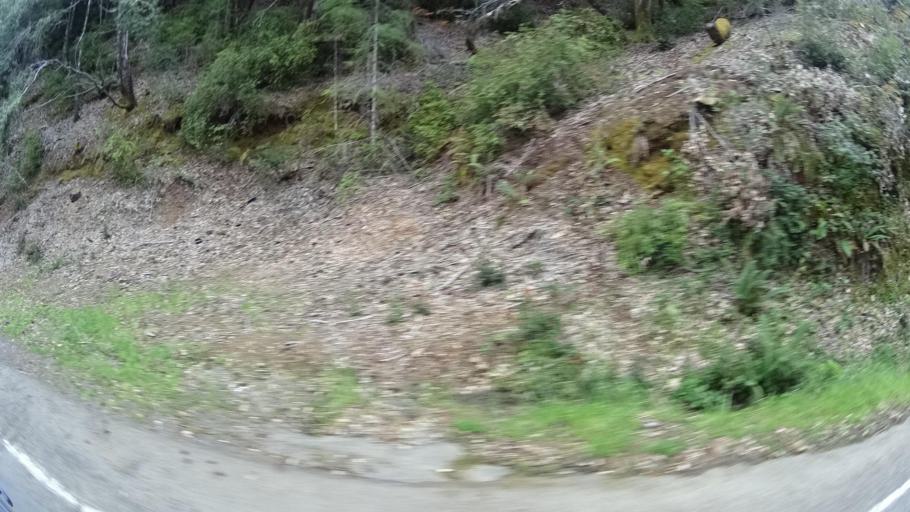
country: US
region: California
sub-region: Humboldt County
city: Redway
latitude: 40.0545
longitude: -123.9857
